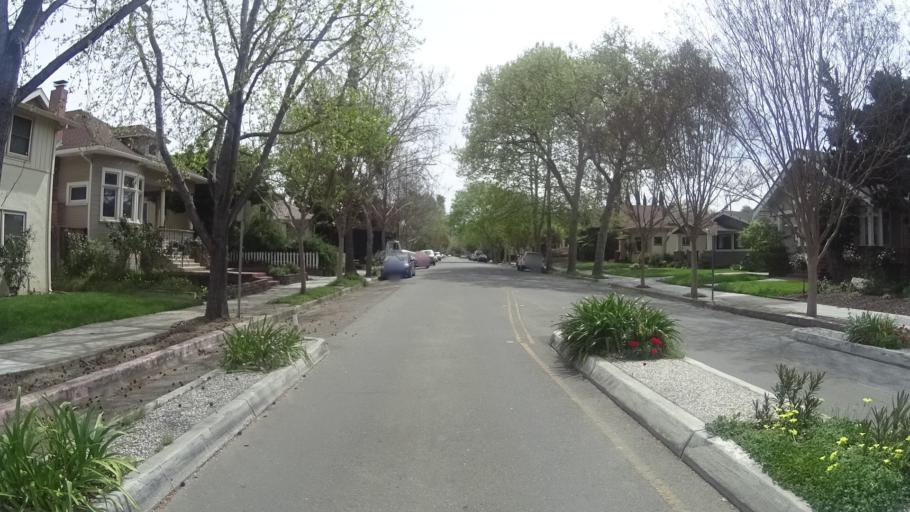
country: US
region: California
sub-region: Santa Clara County
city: San Jose
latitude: 37.3396
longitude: -121.8737
